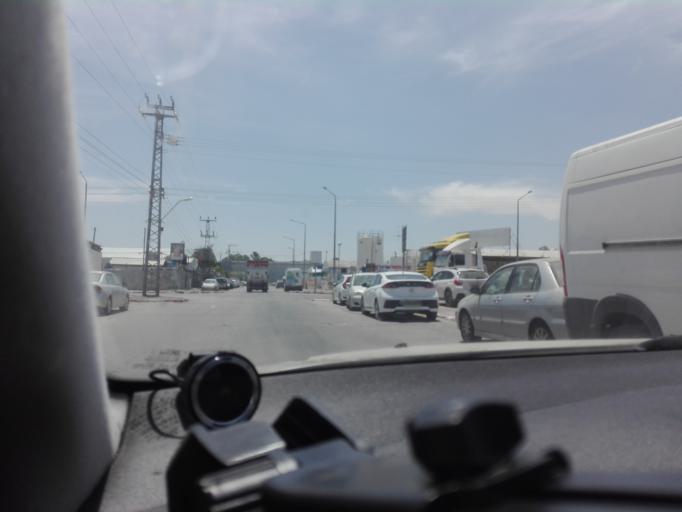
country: IL
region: Central District
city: Bene 'Ayish
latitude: 31.7354
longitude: 34.7545
